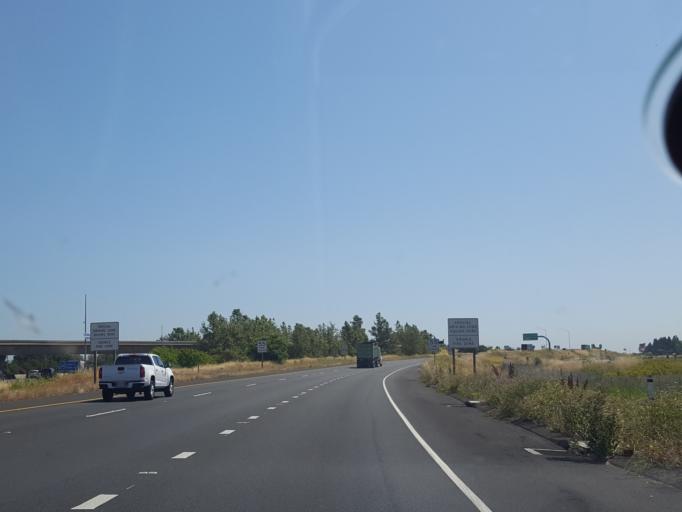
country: US
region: California
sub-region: Solano County
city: Suisun
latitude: 38.2389
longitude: -122.0936
